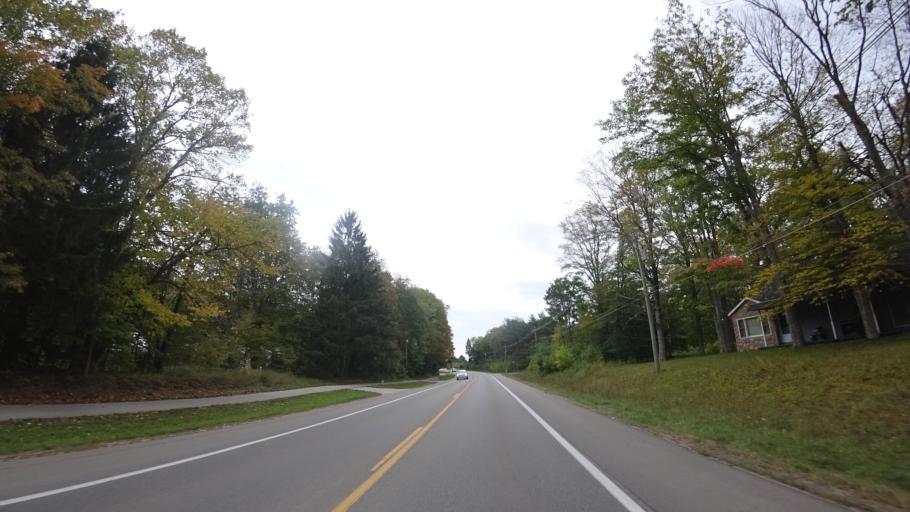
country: US
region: Michigan
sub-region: Emmet County
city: Petoskey
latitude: 45.4284
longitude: -84.9200
